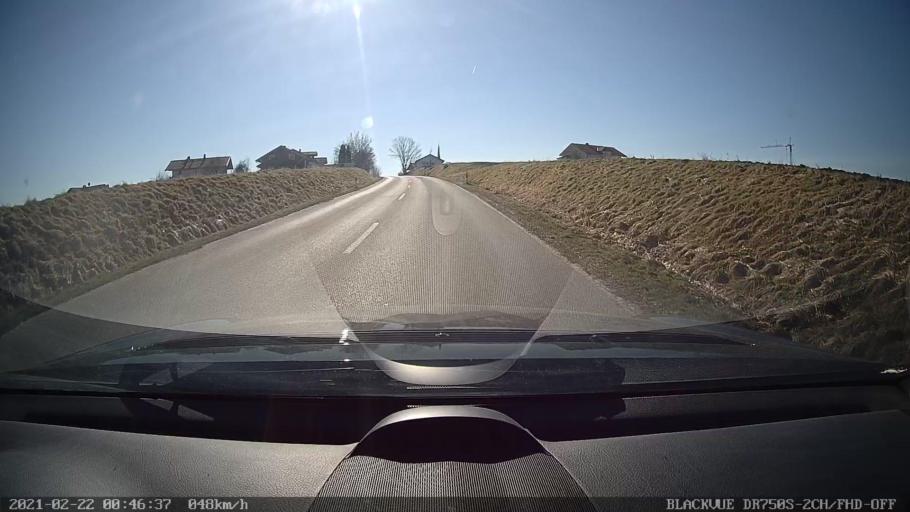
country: DE
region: Bavaria
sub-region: Upper Bavaria
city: Griesstatt
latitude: 47.9990
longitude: 12.1793
